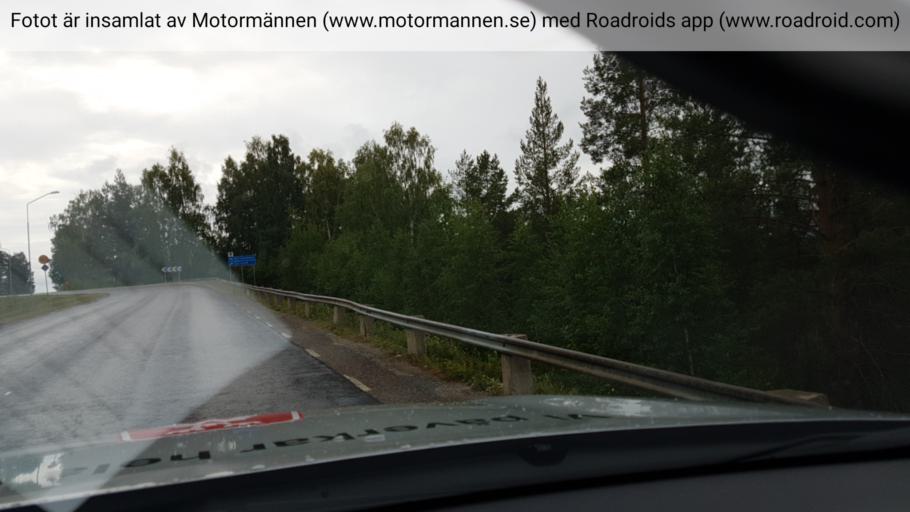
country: SE
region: Norrbotten
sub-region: Alvsbyns Kommun
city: AElvsbyn
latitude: 66.0891
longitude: 20.9469
